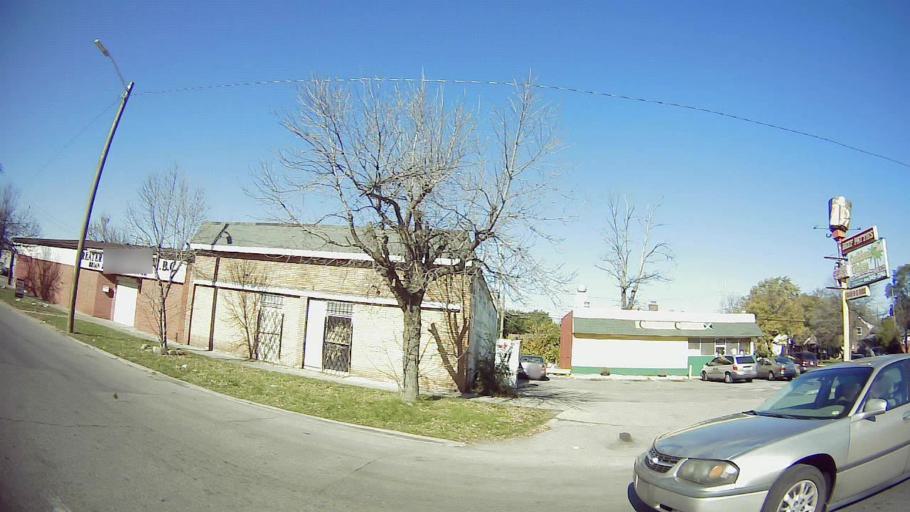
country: US
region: Michigan
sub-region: Oakland County
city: Oak Park
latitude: 42.4168
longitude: -83.1663
